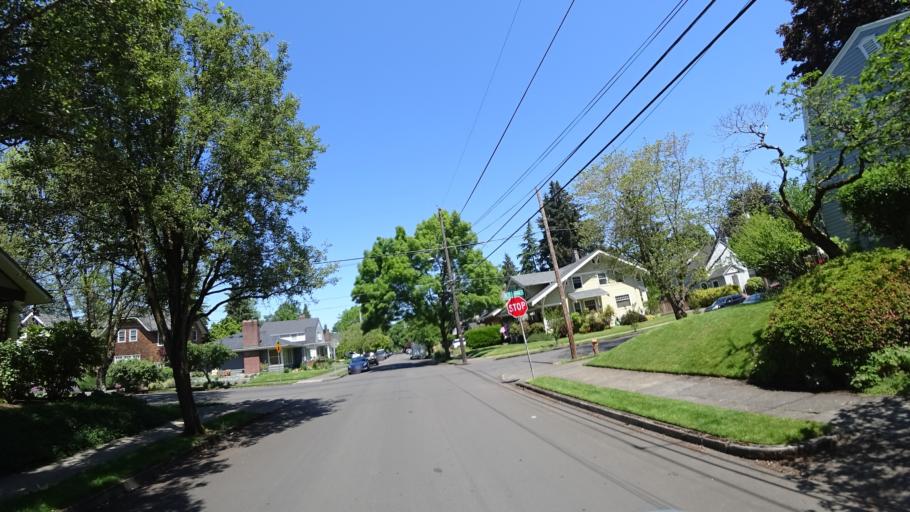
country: US
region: Oregon
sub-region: Multnomah County
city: Portland
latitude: 45.5372
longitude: -122.6382
